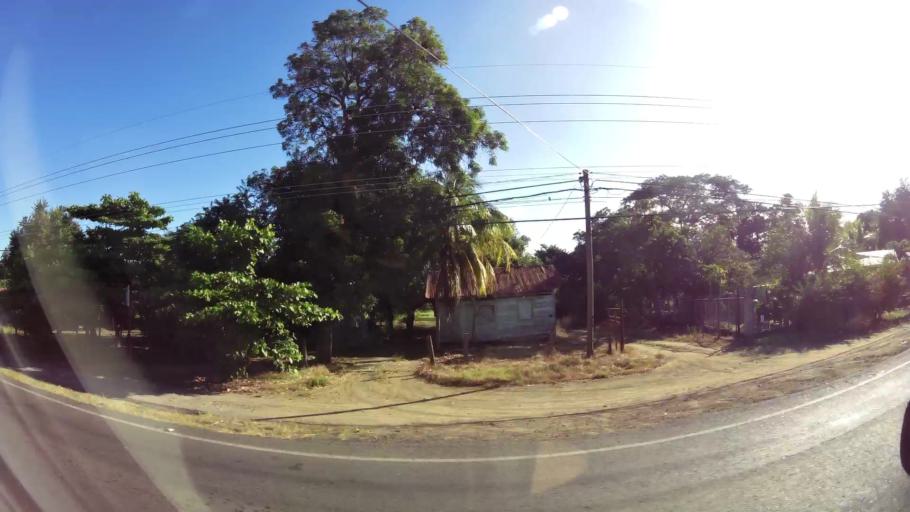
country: CR
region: Guanacaste
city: Belen
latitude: 10.4735
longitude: -85.5628
